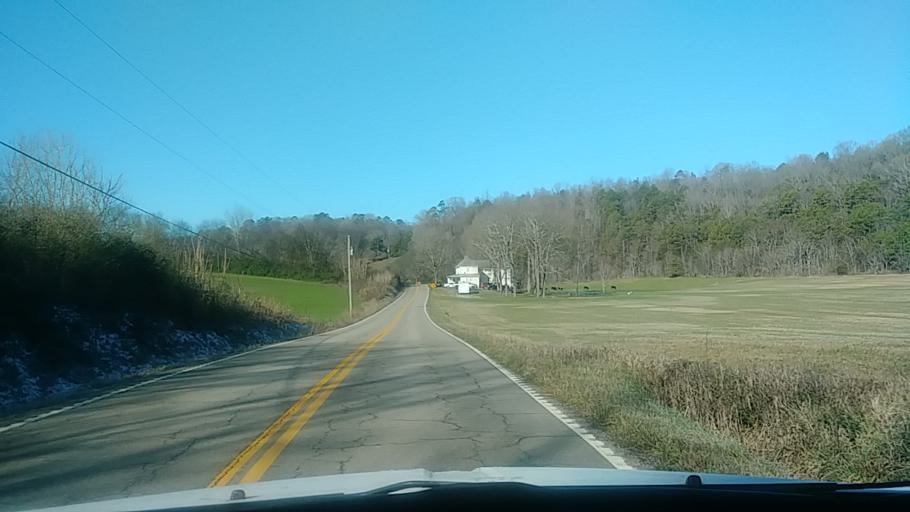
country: US
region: Tennessee
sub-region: Greene County
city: Mosheim
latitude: 36.1275
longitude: -83.0963
